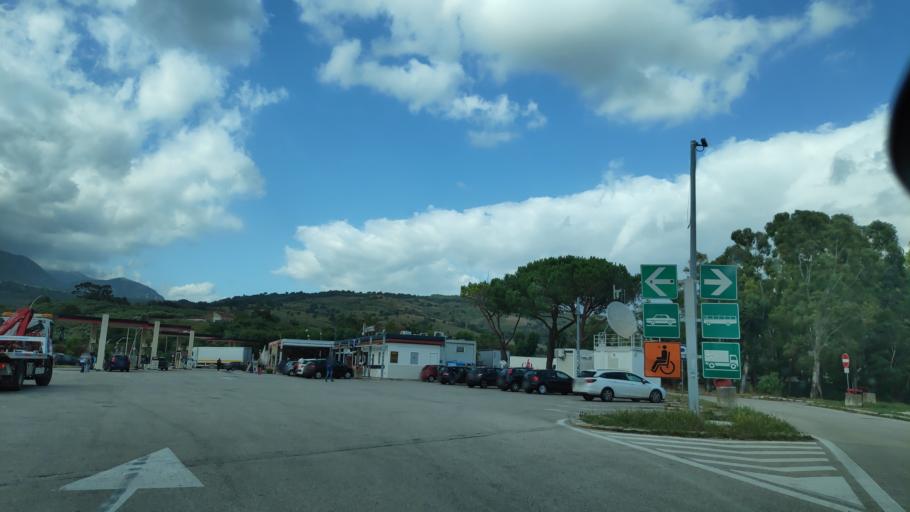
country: IT
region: Campania
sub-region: Provincia di Salerno
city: Serre
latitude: 40.6233
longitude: 15.1825
